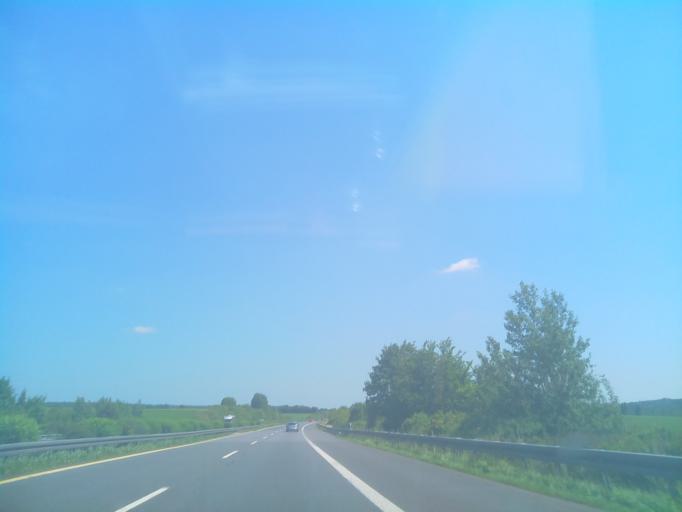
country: DE
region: Baden-Wuerttemberg
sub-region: Regierungsbezirk Stuttgart
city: Grossrinderfeld
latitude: 49.6533
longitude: 9.7431
